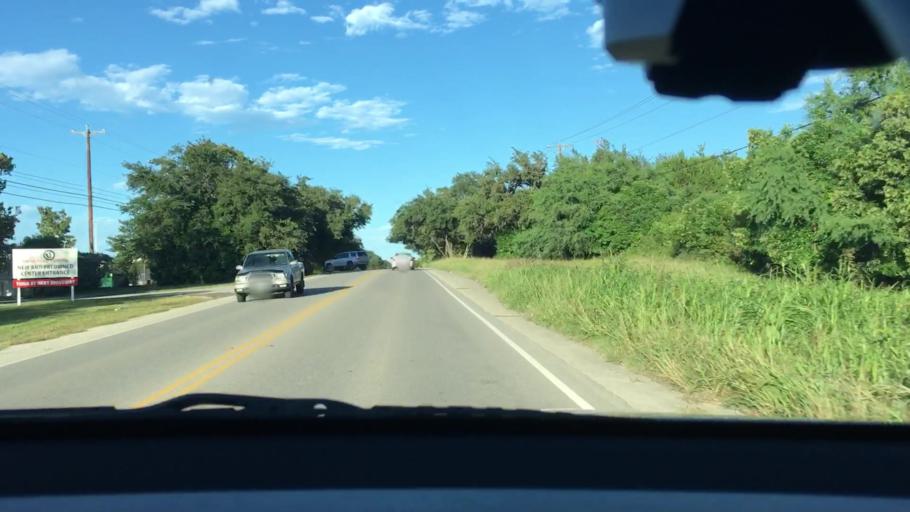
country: US
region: Texas
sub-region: Bexar County
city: Live Oak
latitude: 29.5479
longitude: -98.3605
